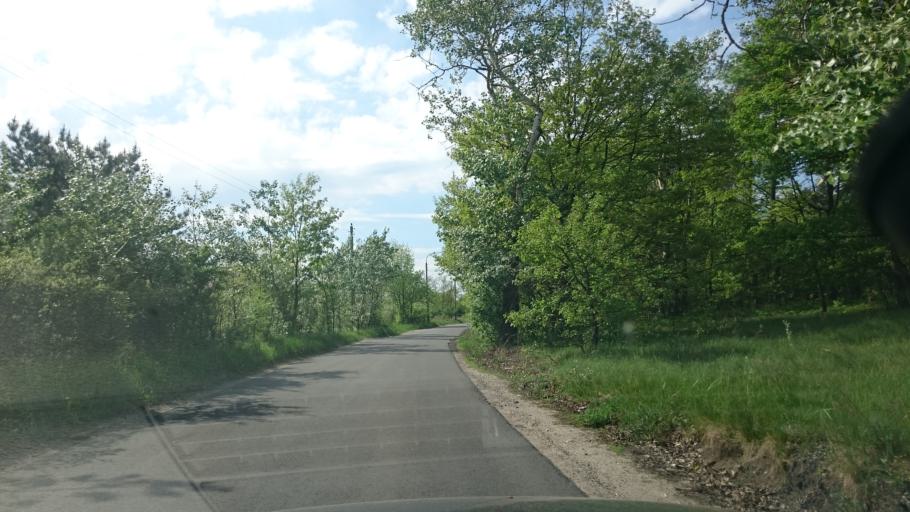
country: PL
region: Kujawsko-Pomorskie
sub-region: Grudziadz
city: Grudziadz
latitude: 53.4562
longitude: 18.7252
